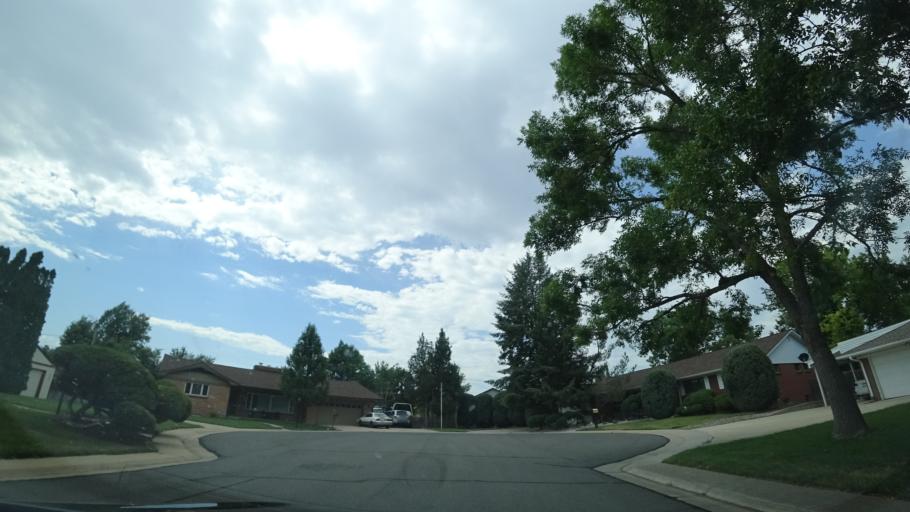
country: US
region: Colorado
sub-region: Jefferson County
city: Lakewood
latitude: 39.7228
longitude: -105.0708
